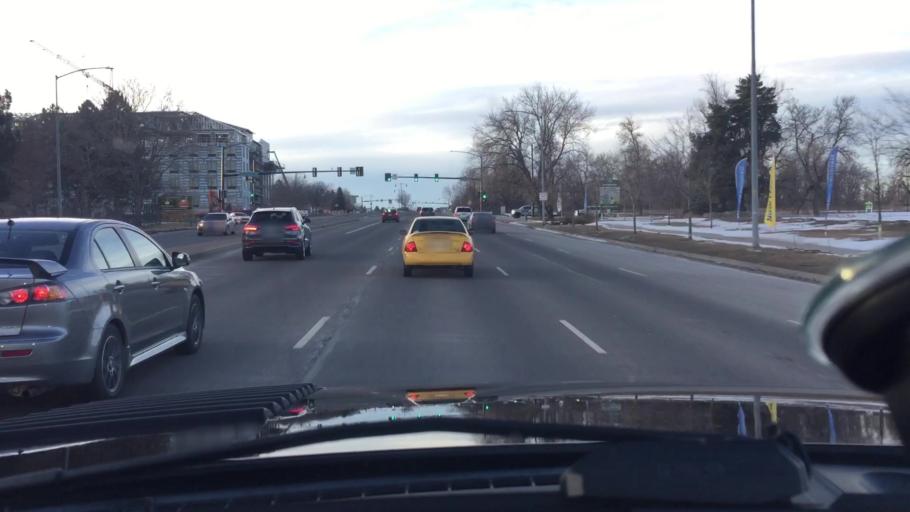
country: US
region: Colorado
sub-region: Adams County
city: Westminster
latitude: 39.8719
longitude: -105.0533
